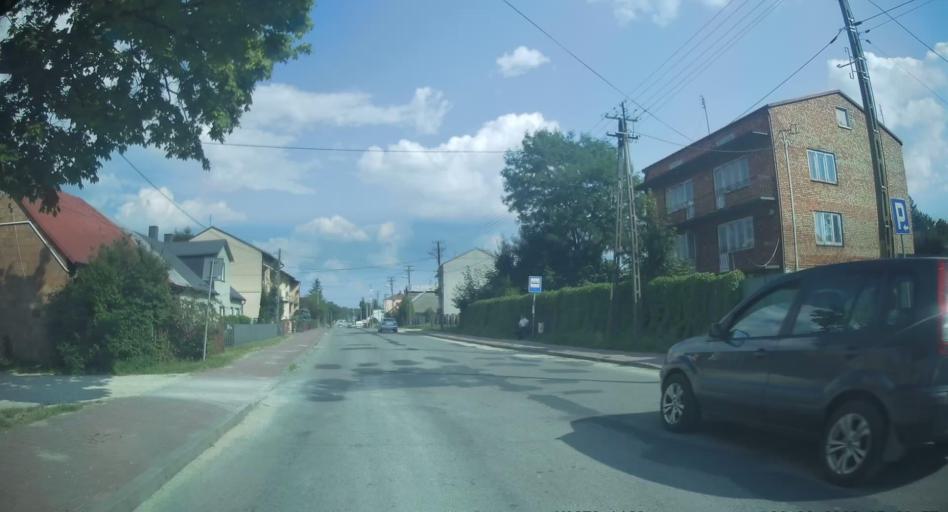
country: PL
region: Swietokrzyskie
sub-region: Powiat konecki
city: Radoszyce
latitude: 51.0732
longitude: 20.2616
